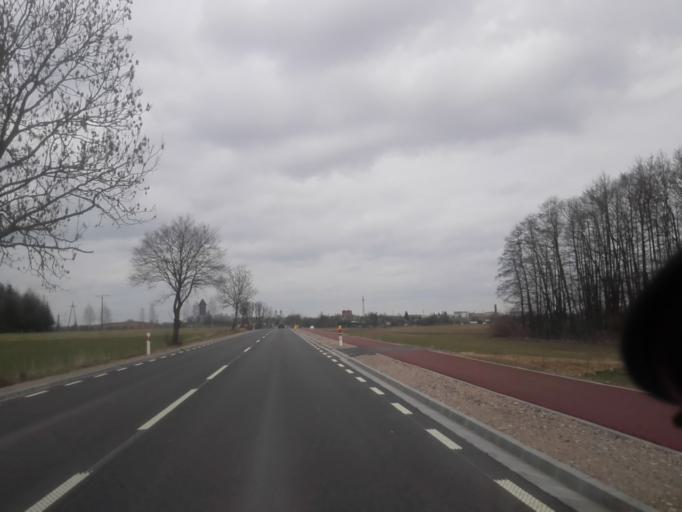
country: PL
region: Podlasie
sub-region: Powiat sejnenski
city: Sejny
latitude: 54.1099
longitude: 23.3228
